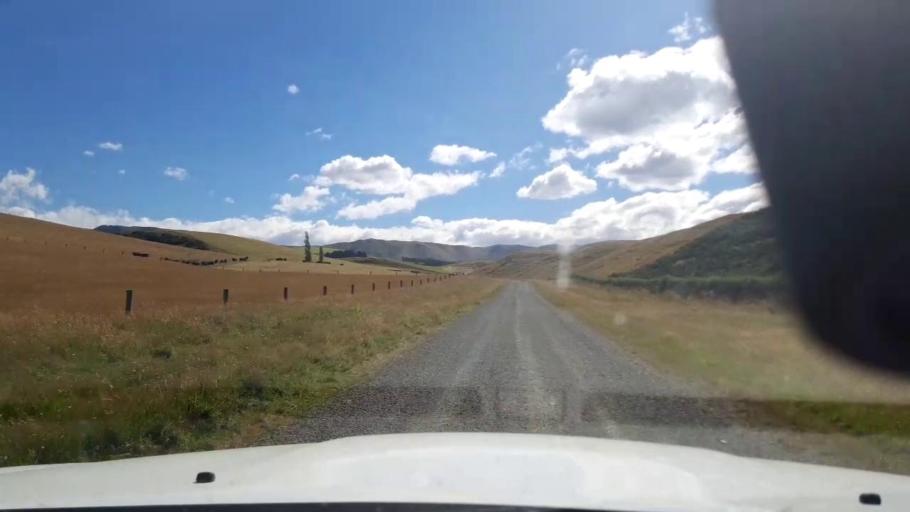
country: NZ
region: Canterbury
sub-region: Timaru District
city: Pleasant Point
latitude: -44.3111
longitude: 170.9000
